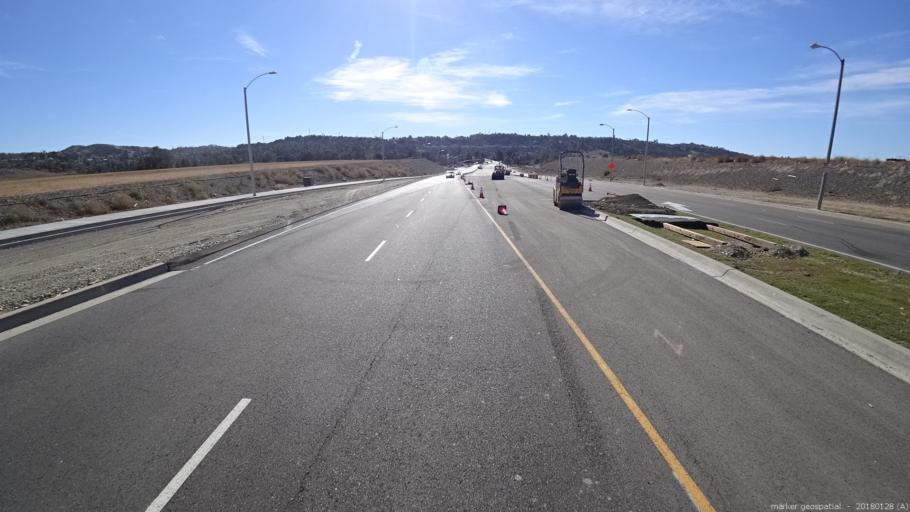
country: US
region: California
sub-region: Los Angeles County
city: Diamond Bar
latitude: 34.0153
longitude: -117.8245
